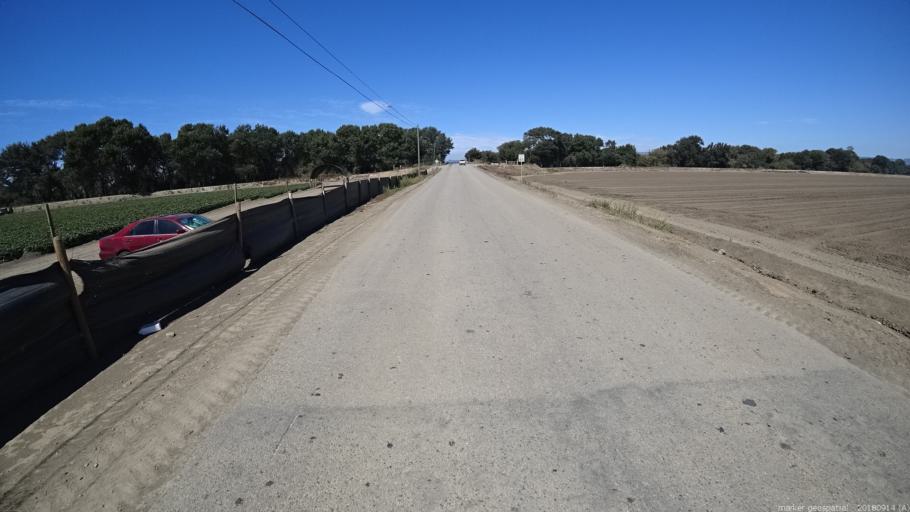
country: US
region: California
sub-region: Santa Cruz County
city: Watsonville
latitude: 36.8782
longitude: -121.7922
